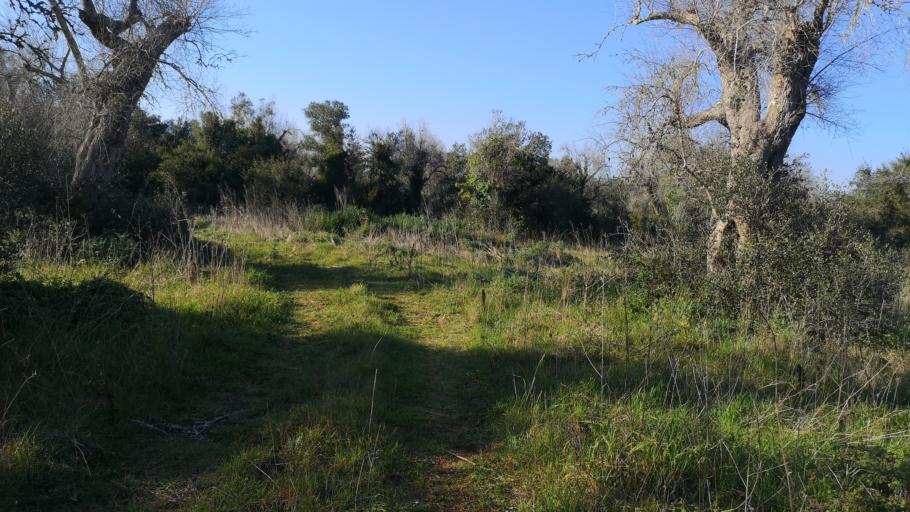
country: IT
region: Apulia
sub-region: Provincia di Lecce
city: Surano
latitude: 40.0079
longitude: 18.3391
